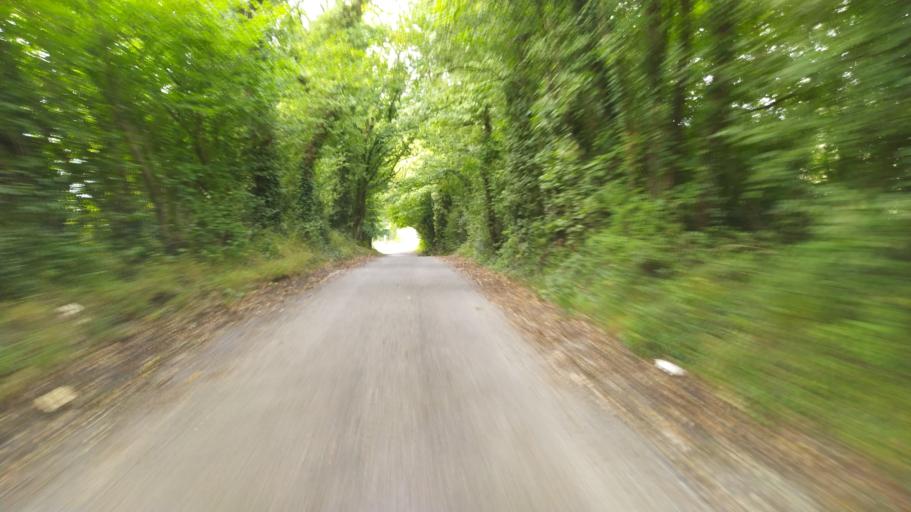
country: GB
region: England
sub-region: Hampshire
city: Long Sutton
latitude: 51.2073
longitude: -0.9006
